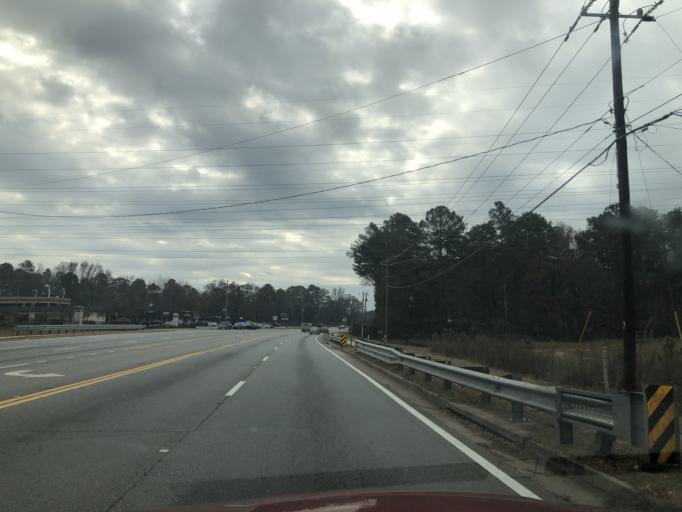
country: US
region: Georgia
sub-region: Clayton County
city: Lake City
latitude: 33.5957
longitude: -84.3375
